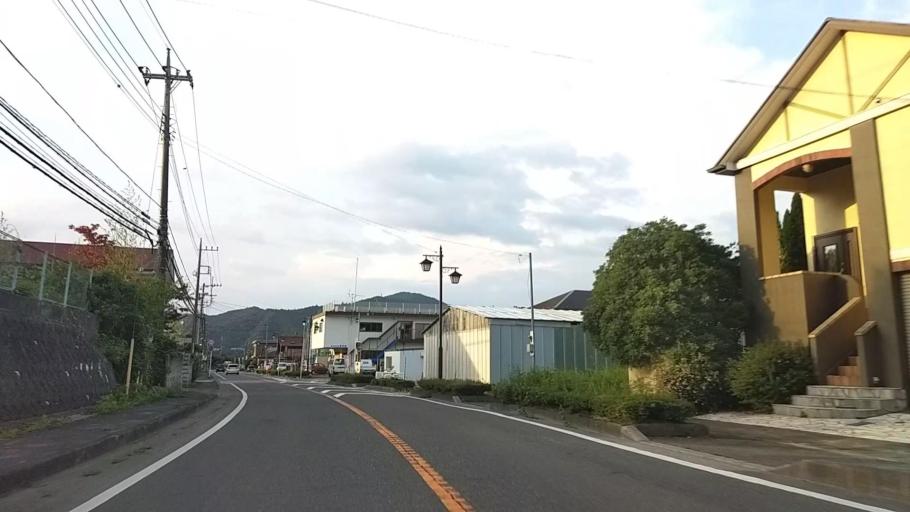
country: JP
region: Kanagawa
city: Hadano
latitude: 35.5195
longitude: 139.2314
